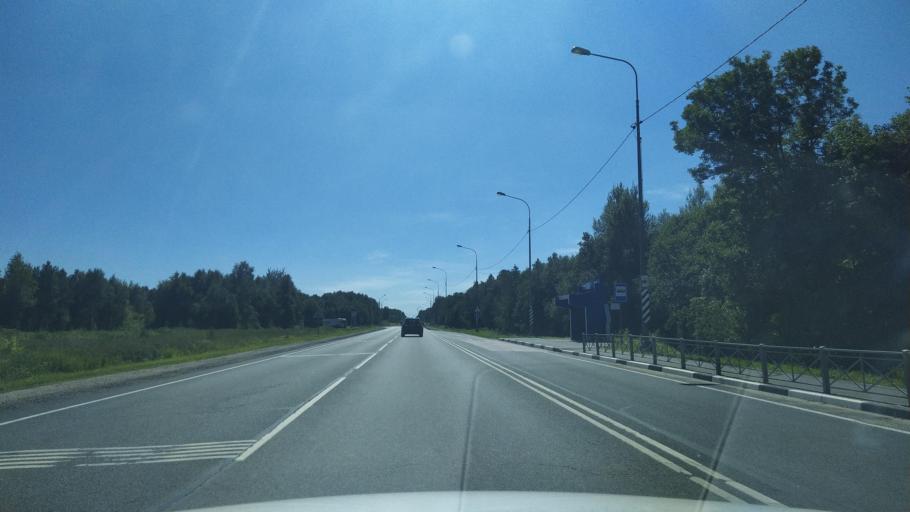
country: RU
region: Pskov
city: Pskov
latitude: 57.7853
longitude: 28.4081
